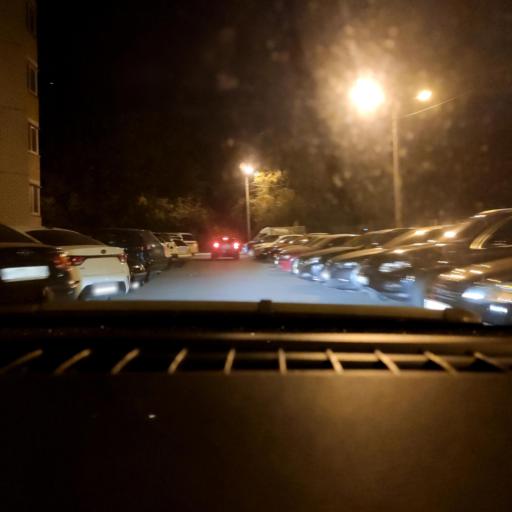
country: RU
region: Voronezj
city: Voronezh
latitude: 51.6821
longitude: 39.2518
